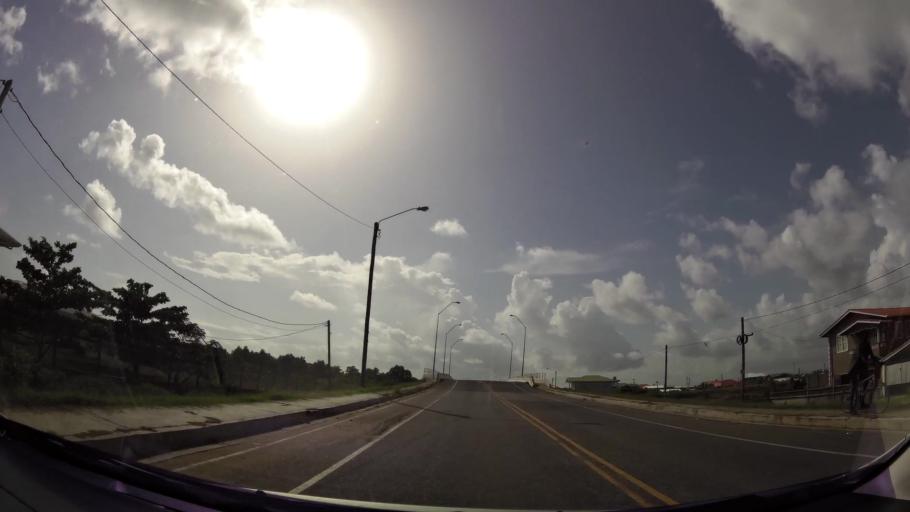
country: GY
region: Demerara-Mahaica
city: Mahaica Village
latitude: 6.7383
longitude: -57.9541
